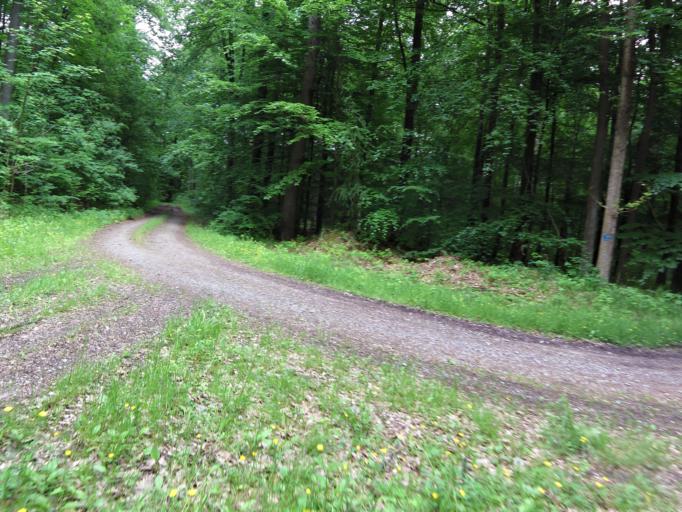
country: DE
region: Bavaria
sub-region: Regierungsbezirk Unterfranken
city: Kleinrinderfeld
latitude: 49.7090
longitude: 9.8199
